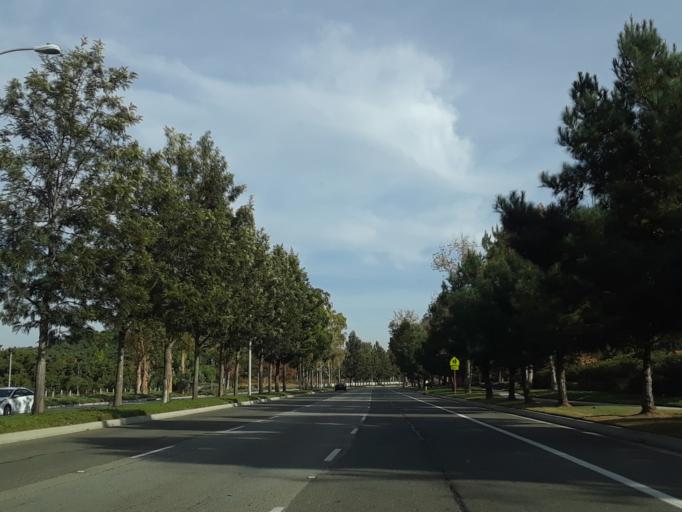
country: US
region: California
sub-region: Orange County
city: North Tustin
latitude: 33.7305
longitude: -117.7567
